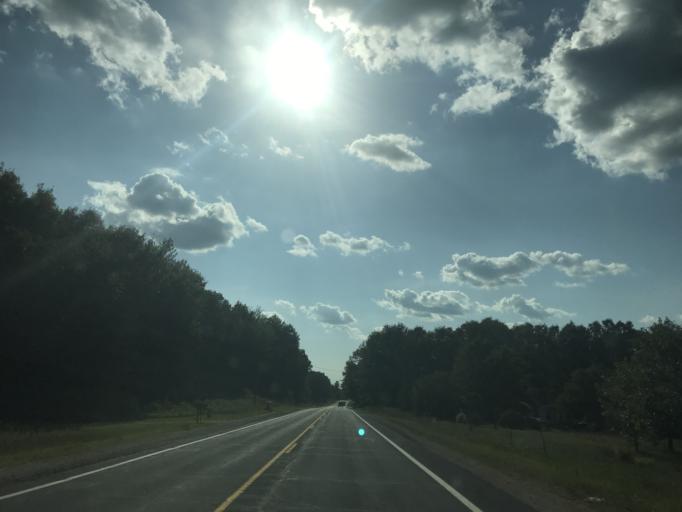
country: US
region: Michigan
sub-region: Newaygo County
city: White Cloud
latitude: 43.5682
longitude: -85.7985
